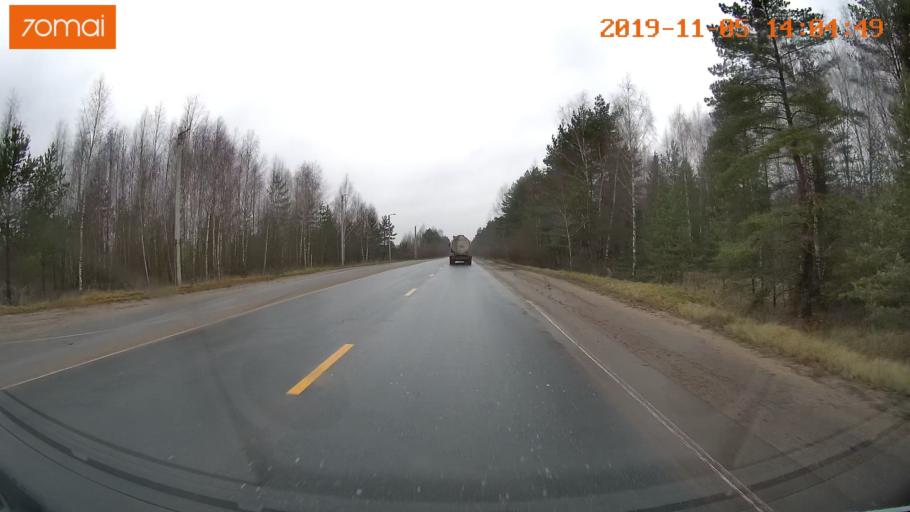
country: RU
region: Ivanovo
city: Kokhma
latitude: 56.9975
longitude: 41.1691
